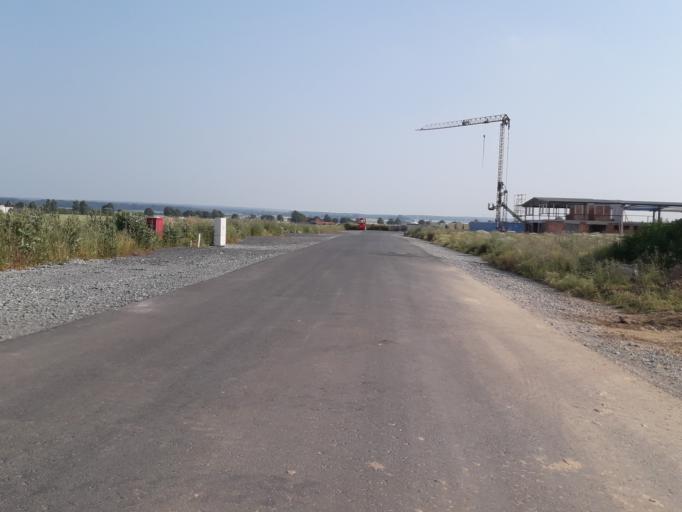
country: DE
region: North Rhine-Westphalia
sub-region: Regierungsbezirk Detmold
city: Salzkotten
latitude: 51.6705
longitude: 8.5793
